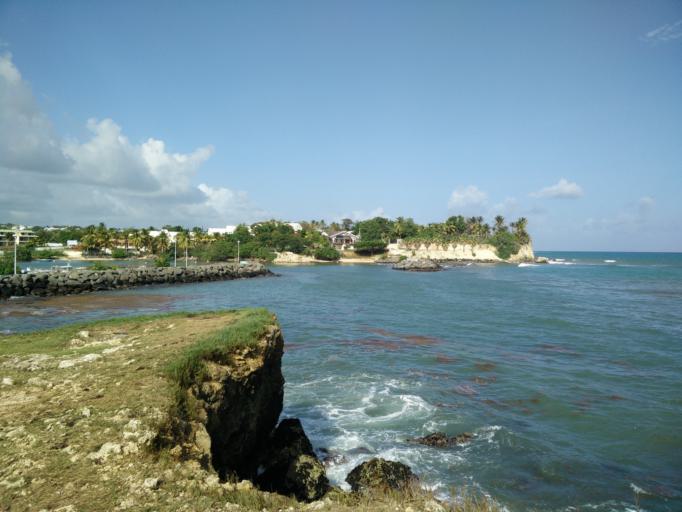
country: GP
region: Guadeloupe
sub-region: Guadeloupe
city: Le Gosier
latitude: 16.2008
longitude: -61.4579
